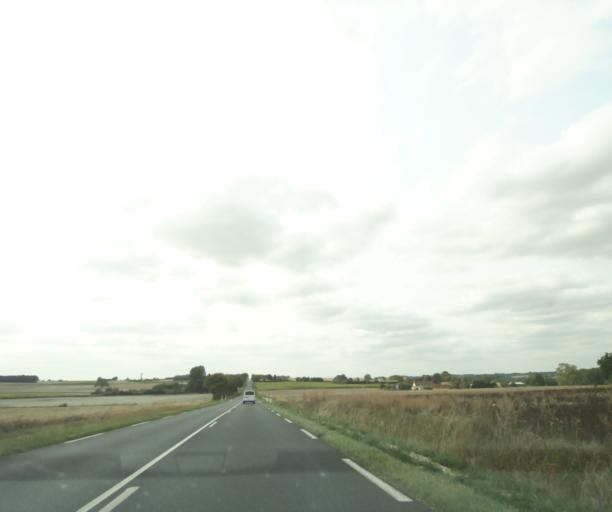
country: FR
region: Centre
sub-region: Departement de l'Indre
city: Clion
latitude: 46.9291
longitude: 1.2748
